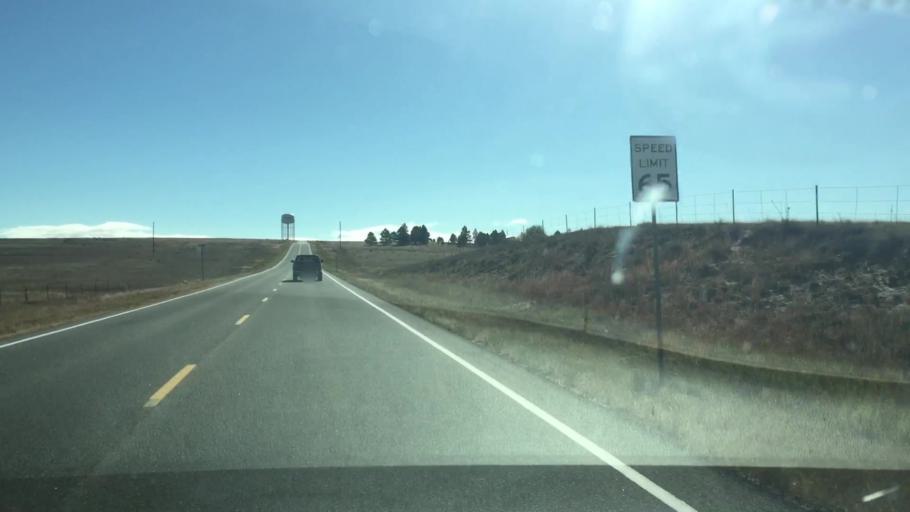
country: US
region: Colorado
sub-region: Elbert County
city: Kiowa
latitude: 39.3436
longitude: -104.4493
